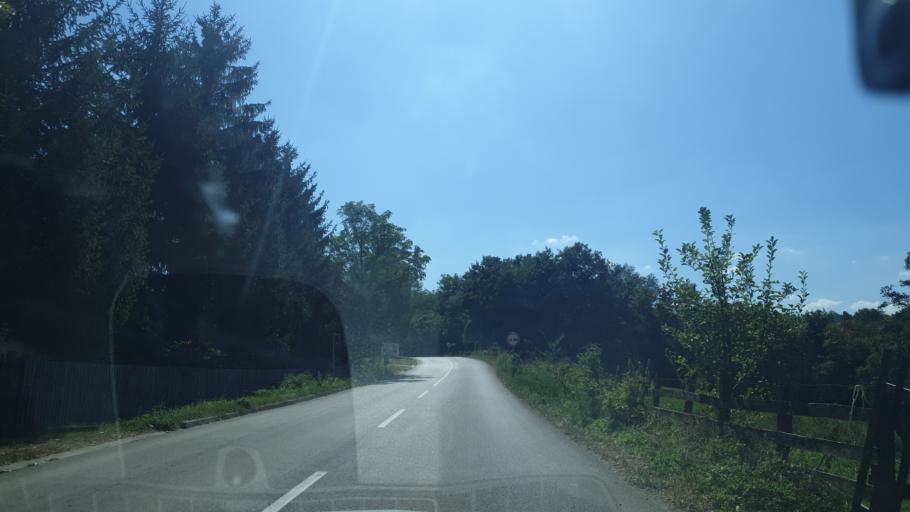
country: RS
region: Central Serbia
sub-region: Kolubarski Okrug
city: Mionica
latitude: 44.1847
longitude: 20.0337
